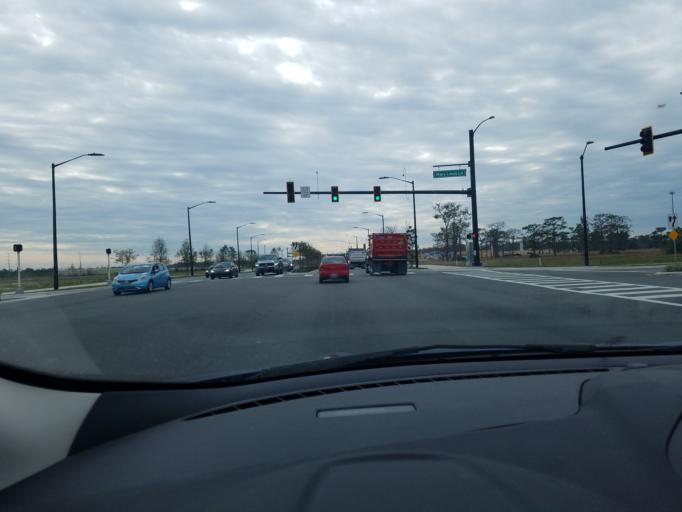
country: US
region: Florida
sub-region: Orange County
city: Hunters Creek
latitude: 28.3483
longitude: -81.3922
